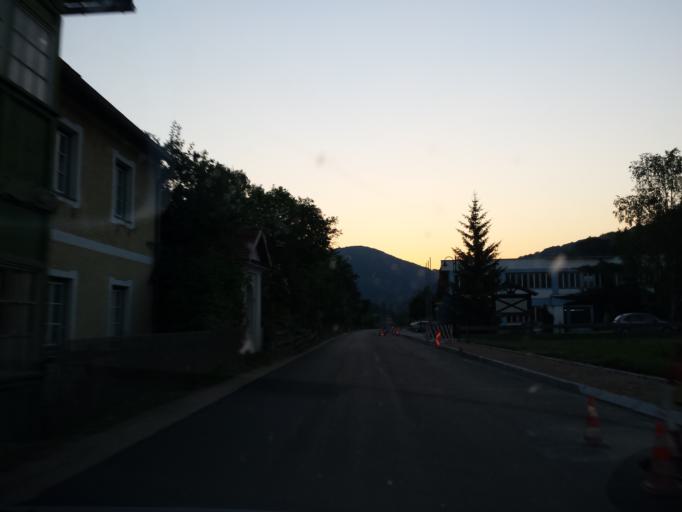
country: AT
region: Lower Austria
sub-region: Politischer Bezirk Lilienfeld
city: Ramsau
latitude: 48.0049
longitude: 15.7987
